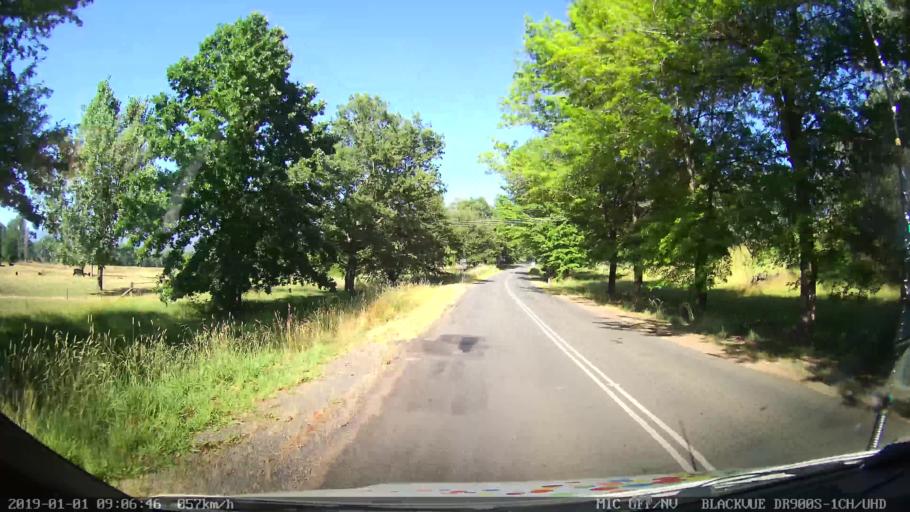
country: AU
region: New South Wales
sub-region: Snowy River
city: Jindabyne
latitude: -36.2172
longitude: 148.1347
